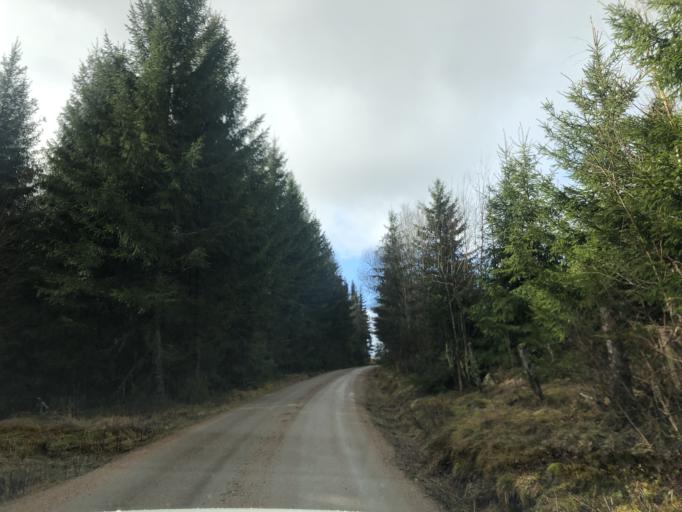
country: SE
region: Vaestra Goetaland
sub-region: Boras Kommun
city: Dalsjofors
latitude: 57.8277
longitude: 13.2288
